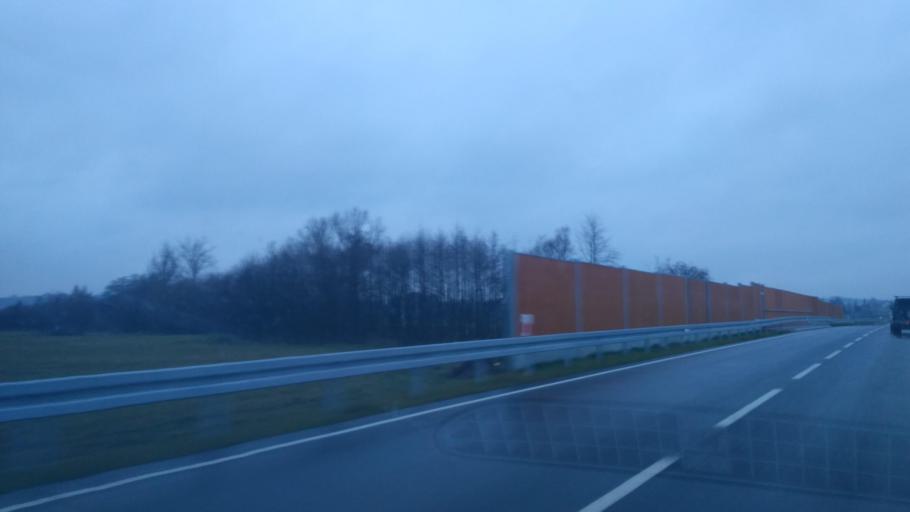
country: PL
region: Subcarpathian Voivodeship
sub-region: Powiat rzeszowski
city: Dynow
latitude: 49.8267
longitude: 22.2418
